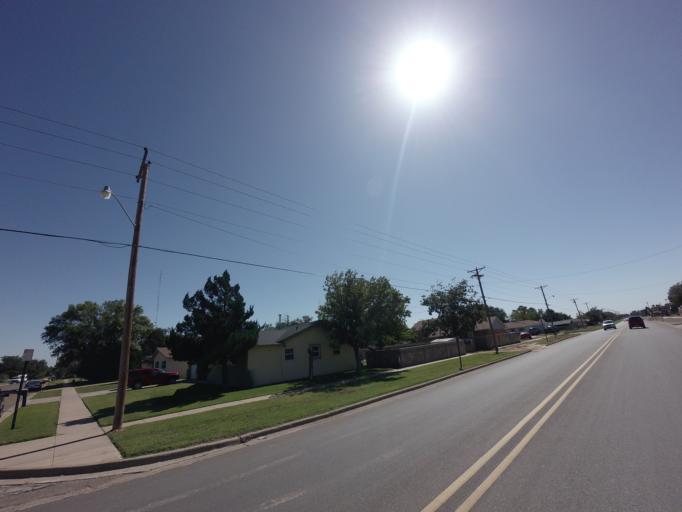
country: US
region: New Mexico
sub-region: Curry County
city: Clovis
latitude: 34.4175
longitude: -103.2142
